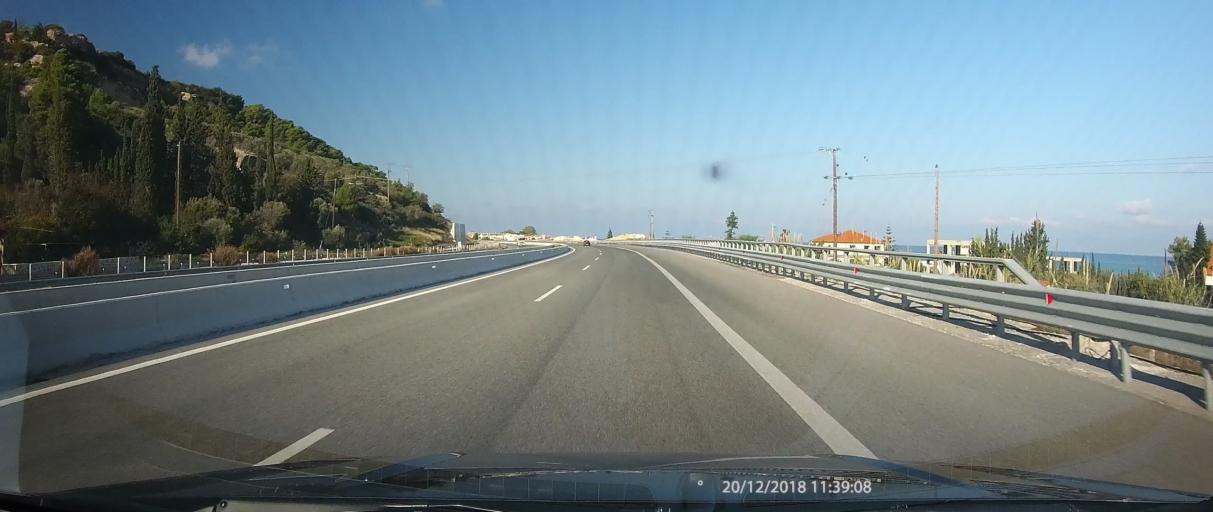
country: GR
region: Peloponnese
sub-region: Nomos Korinthias
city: Kato Dhiminio
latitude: 38.0384
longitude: 22.7096
